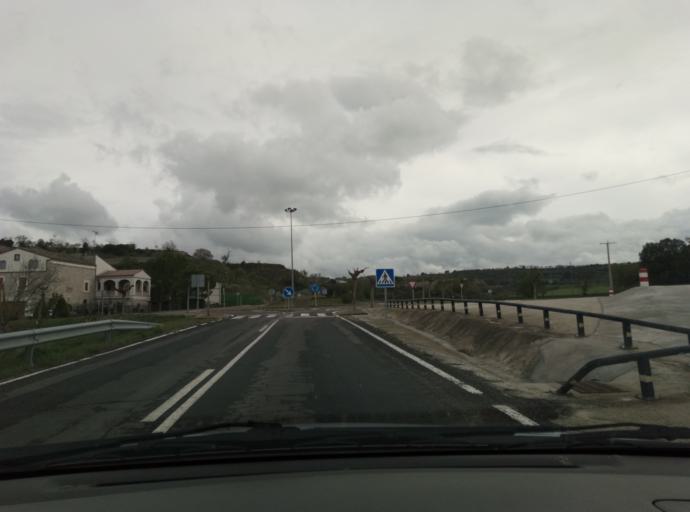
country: ES
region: Catalonia
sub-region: Provincia de Lleida
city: Cervera
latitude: 41.6263
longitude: 1.3396
